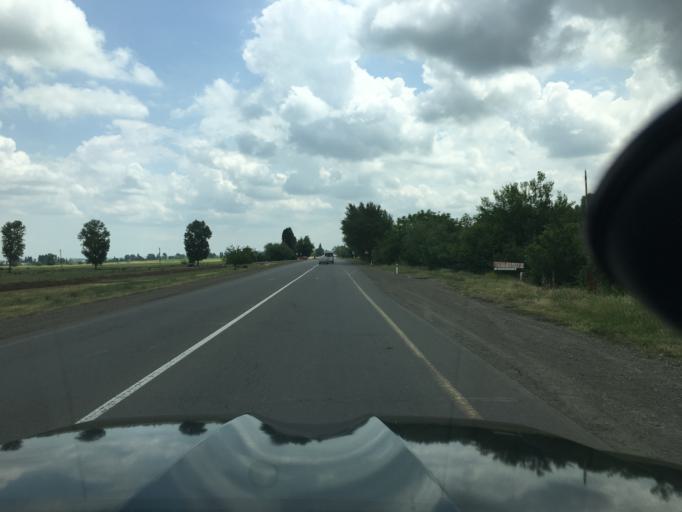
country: AZ
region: Tovuz
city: Tovuz
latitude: 40.9573
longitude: 45.7311
